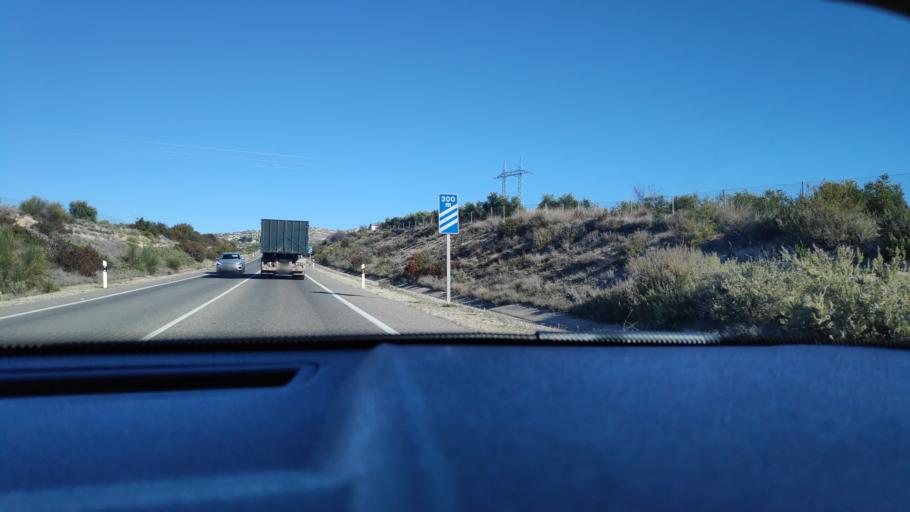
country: ES
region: Andalusia
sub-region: Province of Cordoba
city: Baena
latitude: 37.6168
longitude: -4.3007
